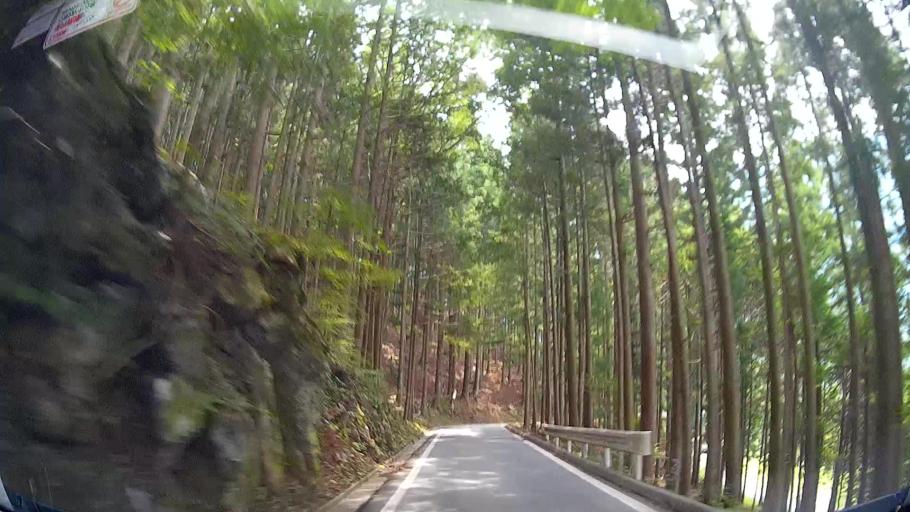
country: JP
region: Nagano
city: Iida
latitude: 35.2865
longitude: 137.9212
